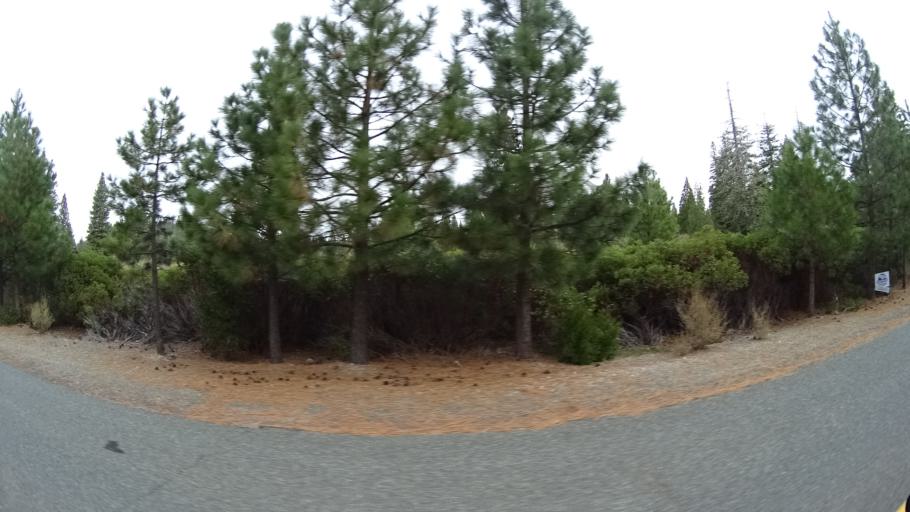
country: US
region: California
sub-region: Siskiyou County
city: Weed
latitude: 41.4078
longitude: -122.3692
